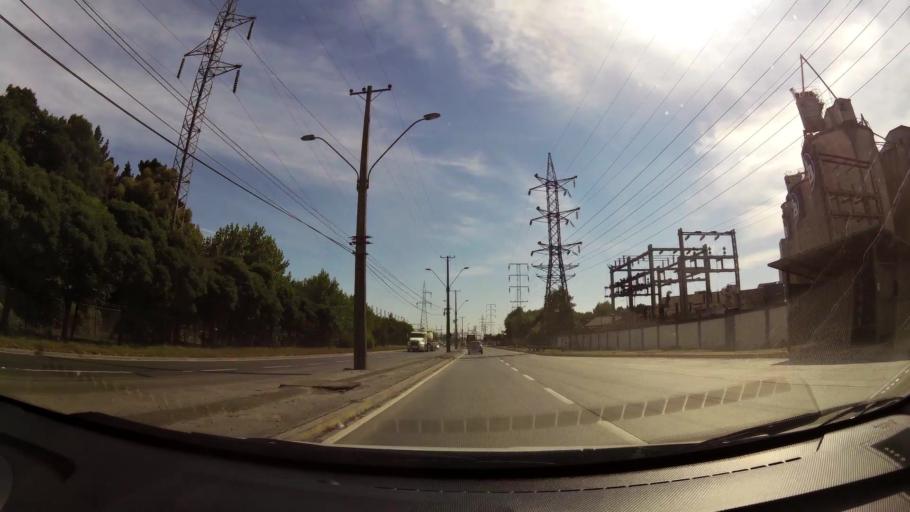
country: CL
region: Biobio
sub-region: Provincia de Concepcion
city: Talcahuano
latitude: -36.7433
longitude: -73.1206
